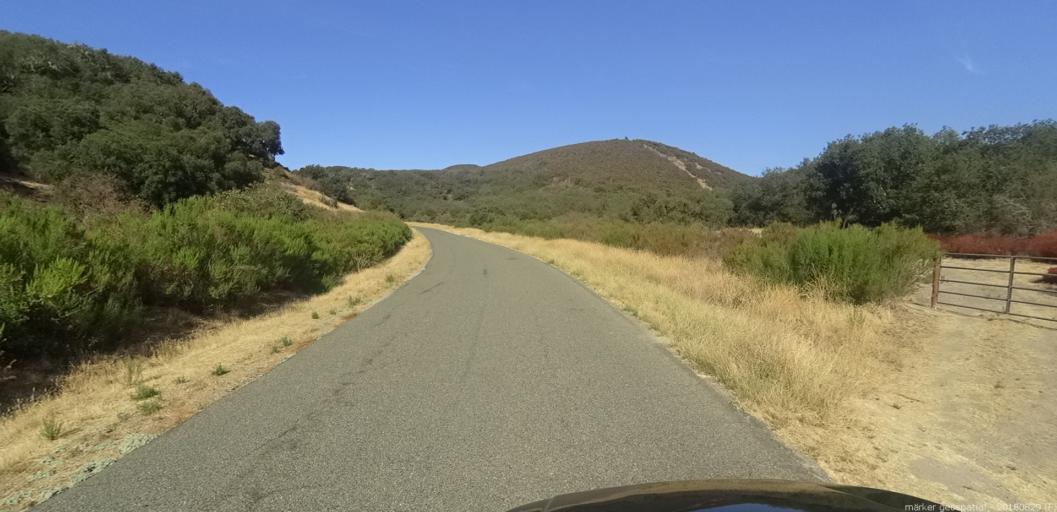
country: US
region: California
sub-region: Monterey County
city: King City
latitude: 36.0477
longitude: -121.0579
